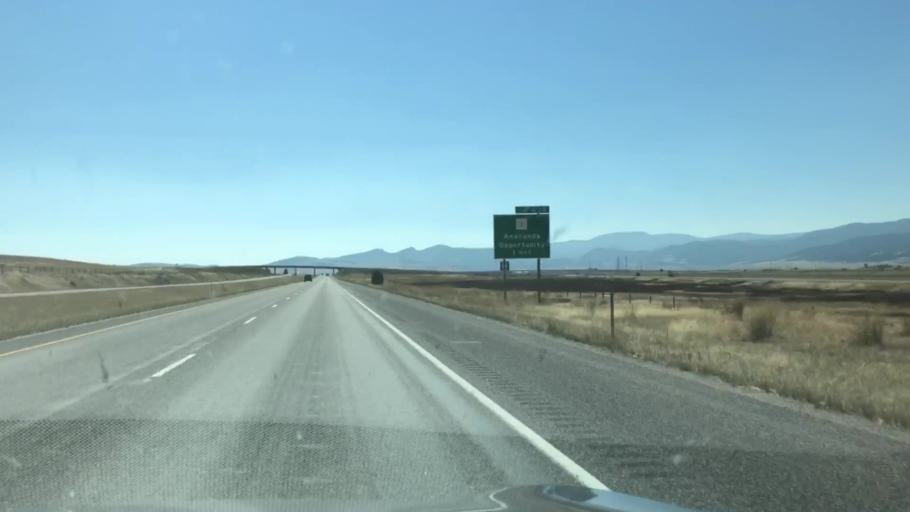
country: US
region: Montana
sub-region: Deer Lodge County
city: Warm Springs
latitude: 46.1136
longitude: -112.8005
